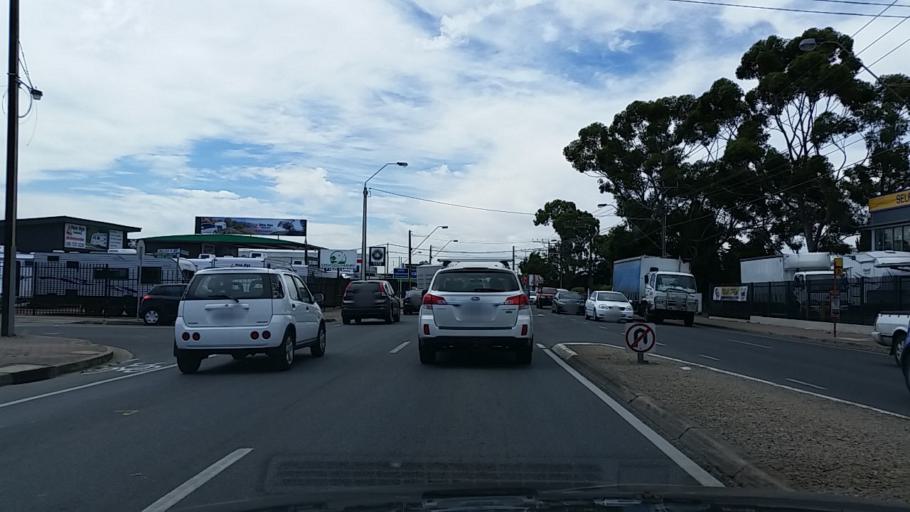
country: AU
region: South Australia
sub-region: Marion
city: Clovelly Park
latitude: -34.9972
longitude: 138.5752
